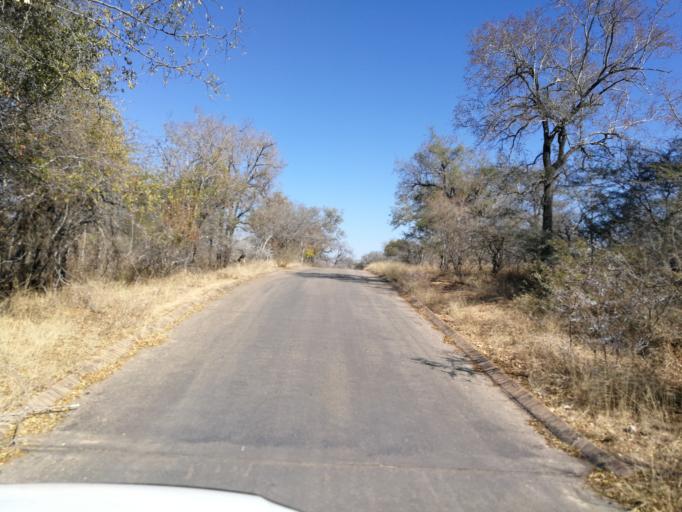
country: ZA
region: Limpopo
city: Thulamahashi
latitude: -24.9834
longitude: 31.5775
